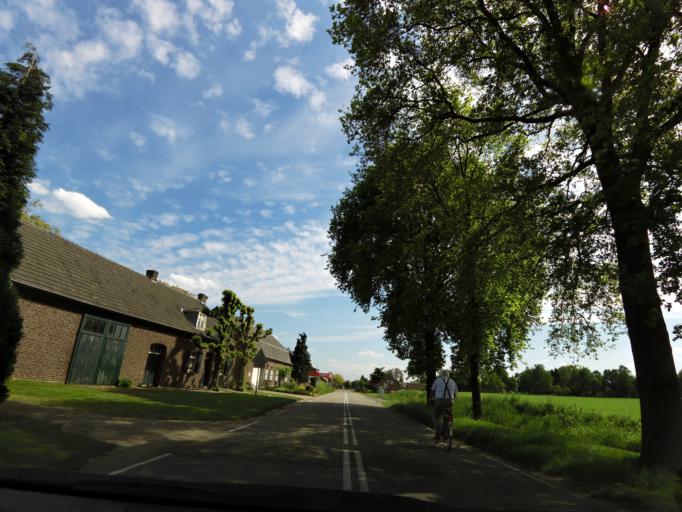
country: NL
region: Limburg
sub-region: Gemeente Leudal
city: Haelen
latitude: 51.2668
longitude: 5.9847
